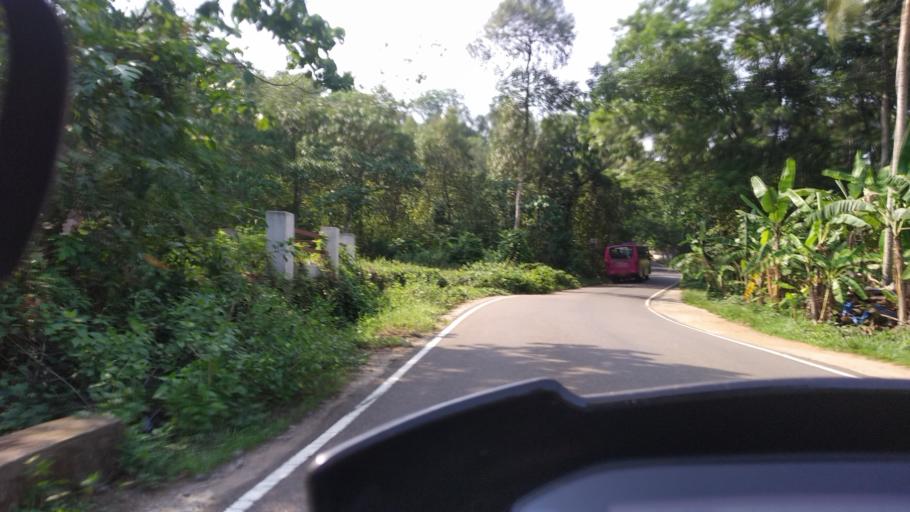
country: IN
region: Kerala
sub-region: Ernakulam
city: Piravam
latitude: 9.8149
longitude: 76.5600
